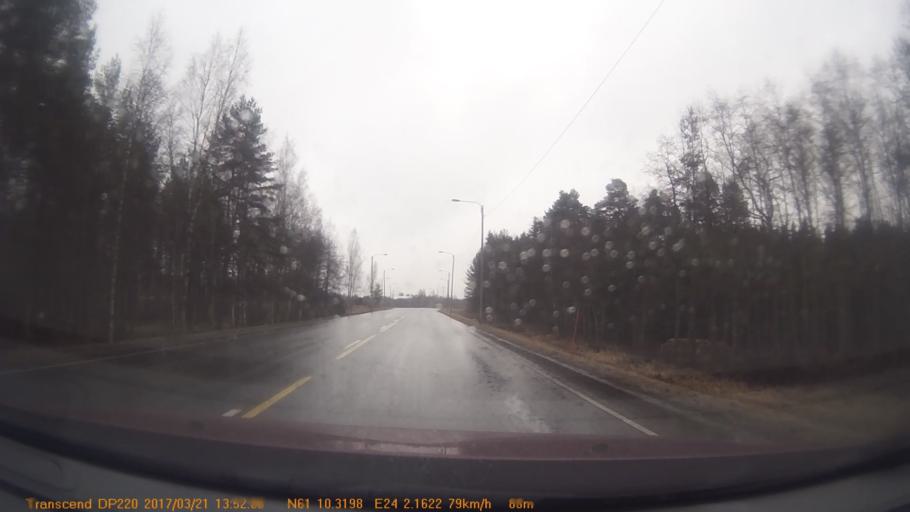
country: FI
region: Pirkanmaa
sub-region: Etelae-Pirkanmaa
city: Valkeakoski
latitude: 61.1724
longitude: 24.0360
